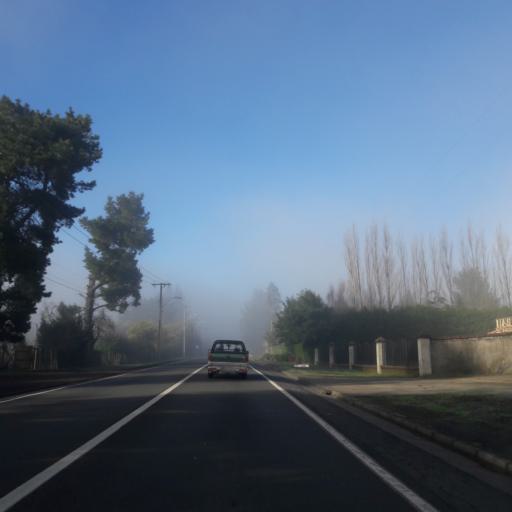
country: CL
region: Biobio
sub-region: Provincia de Concepcion
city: Chiguayante
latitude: -37.0153
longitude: -72.9872
